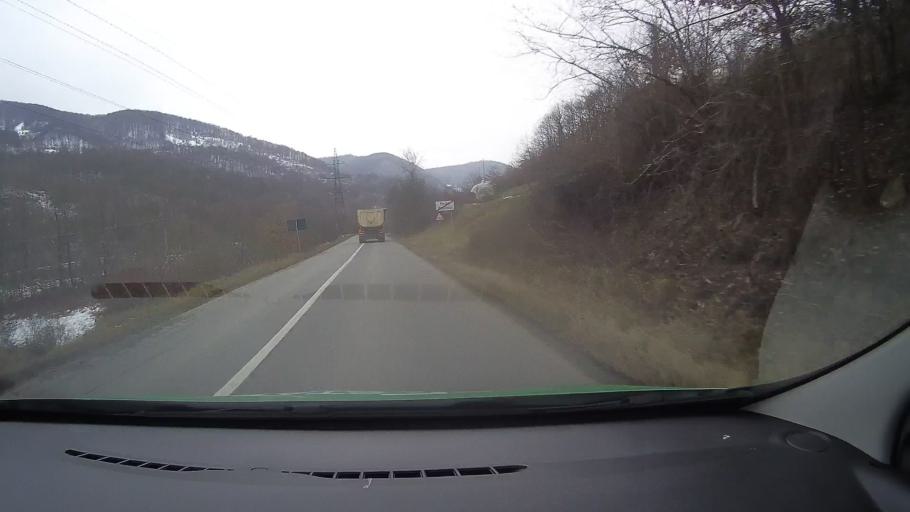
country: RO
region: Alba
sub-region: Comuna Metes
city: Metes
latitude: 46.0918
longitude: 23.3728
